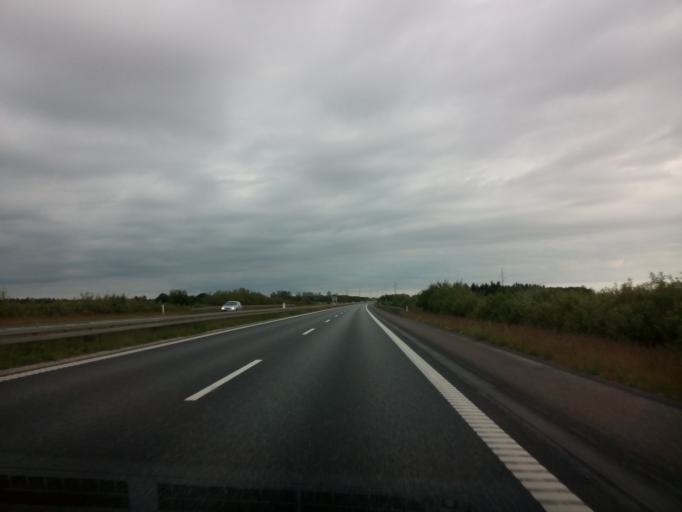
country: DK
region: North Denmark
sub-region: Hjorring Kommune
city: Vra
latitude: 57.3479
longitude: 10.0303
